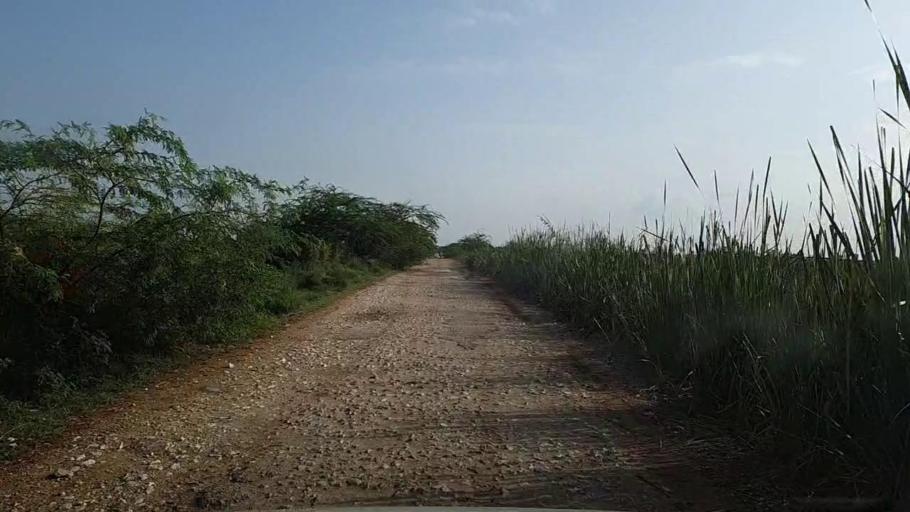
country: PK
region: Sindh
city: Pad Idan
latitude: 26.8154
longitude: 68.2374
